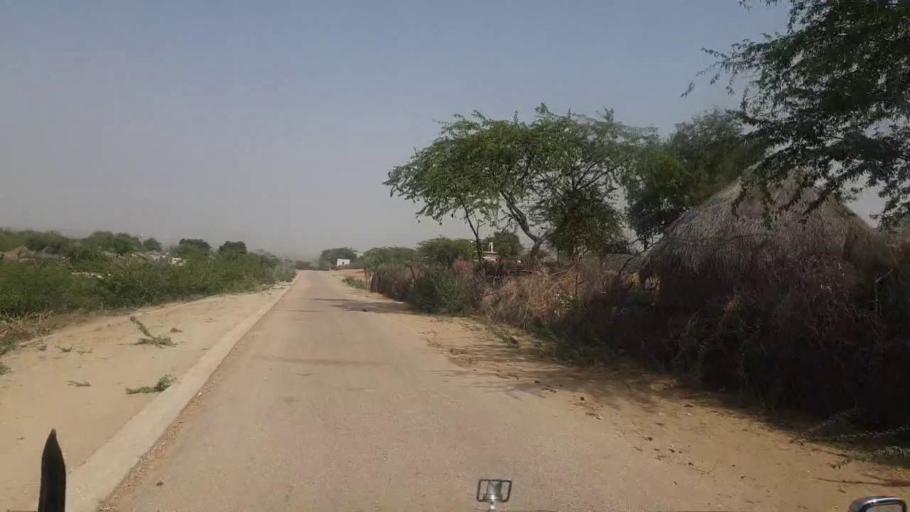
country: PK
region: Sindh
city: Umarkot
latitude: 25.2300
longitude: 70.2450
